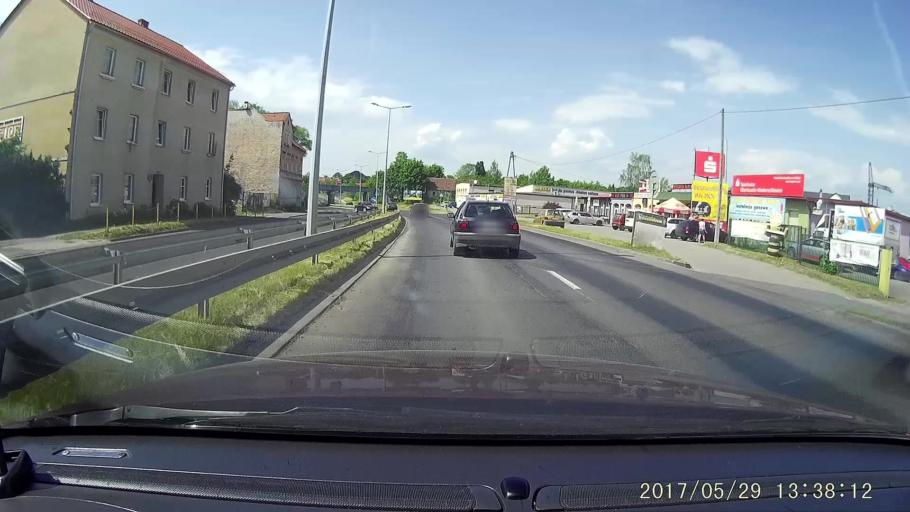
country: PL
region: Lower Silesian Voivodeship
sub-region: Powiat lubanski
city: Luban
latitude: 51.1212
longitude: 15.2953
